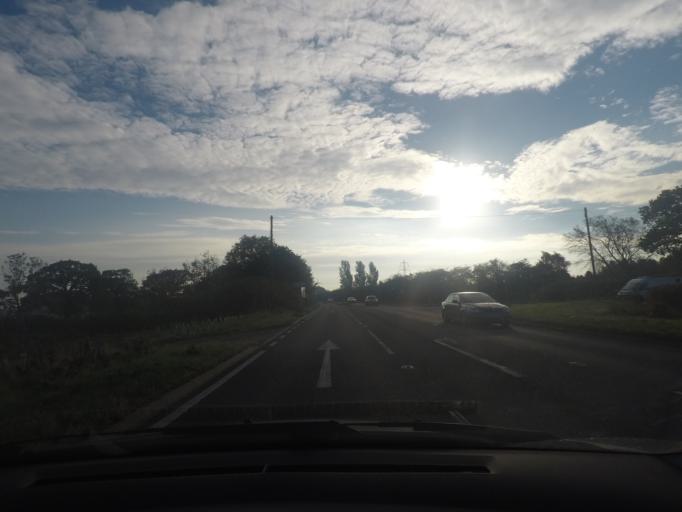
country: GB
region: England
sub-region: City of York
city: Elvington
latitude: 53.9505
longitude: -0.9427
